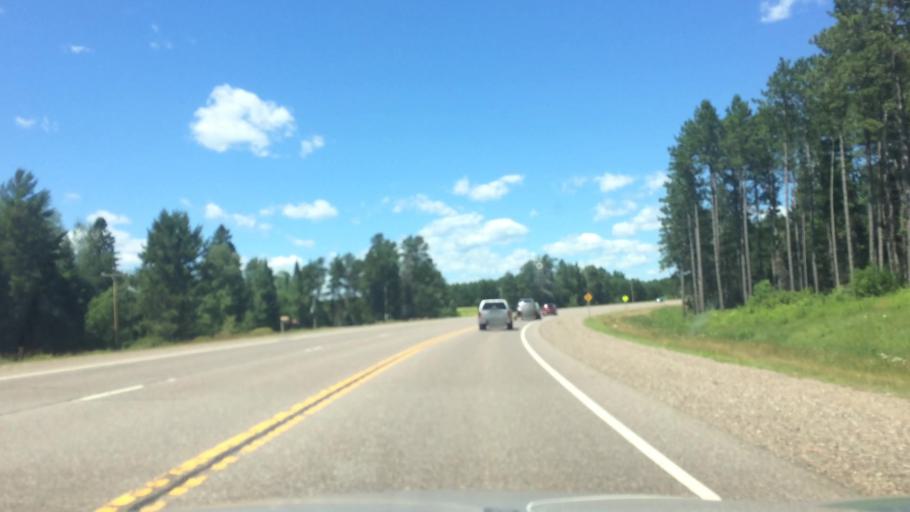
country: US
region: Wisconsin
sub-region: Lincoln County
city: Tomahawk
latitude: 45.6630
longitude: -89.7121
